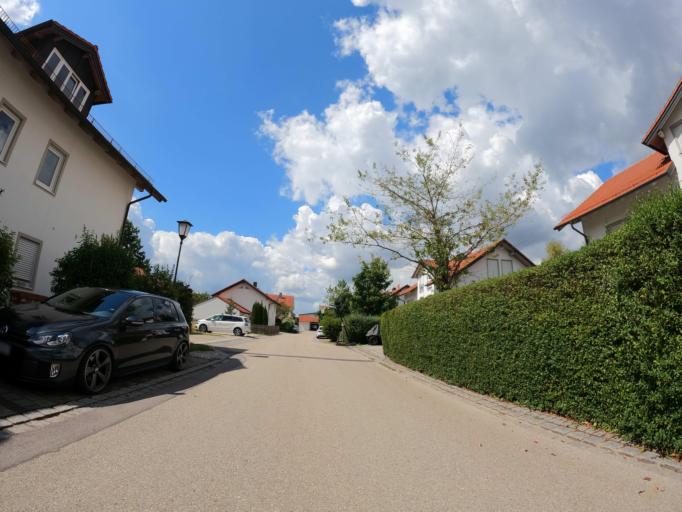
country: DE
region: Bavaria
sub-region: Upper Bavaria
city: Brunnthal
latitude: 48.0081
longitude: 11.6794
